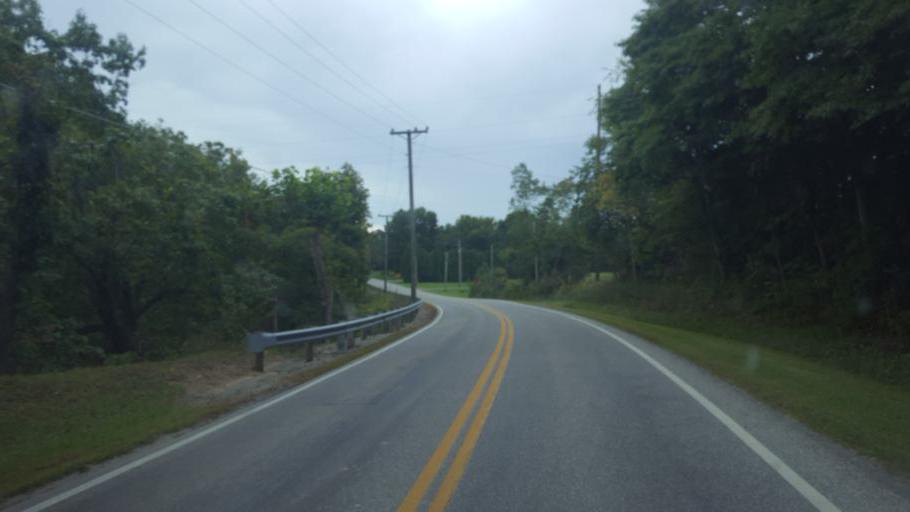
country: US
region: Ohio
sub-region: Delaware County
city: Sunbury
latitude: 40.2547
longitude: -82.8455
